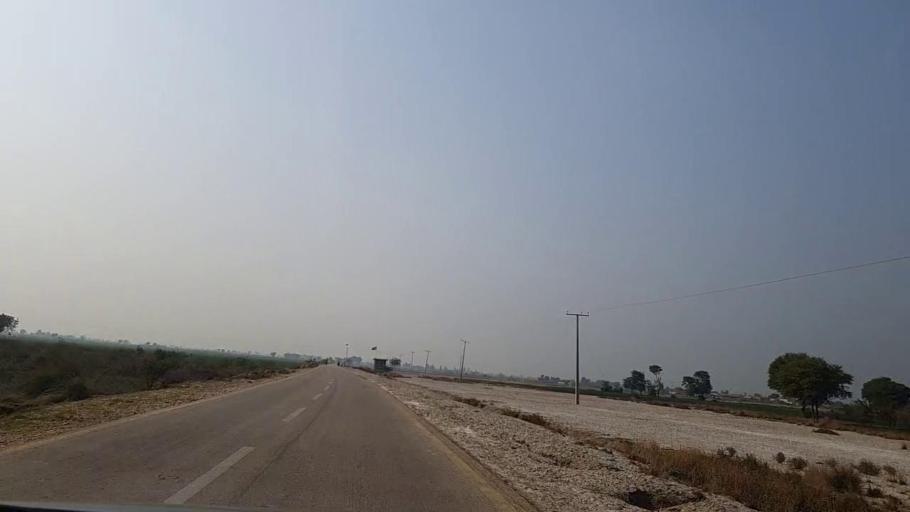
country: PK
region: Sindh
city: Sakrand
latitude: 26.1360
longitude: 68.1865
